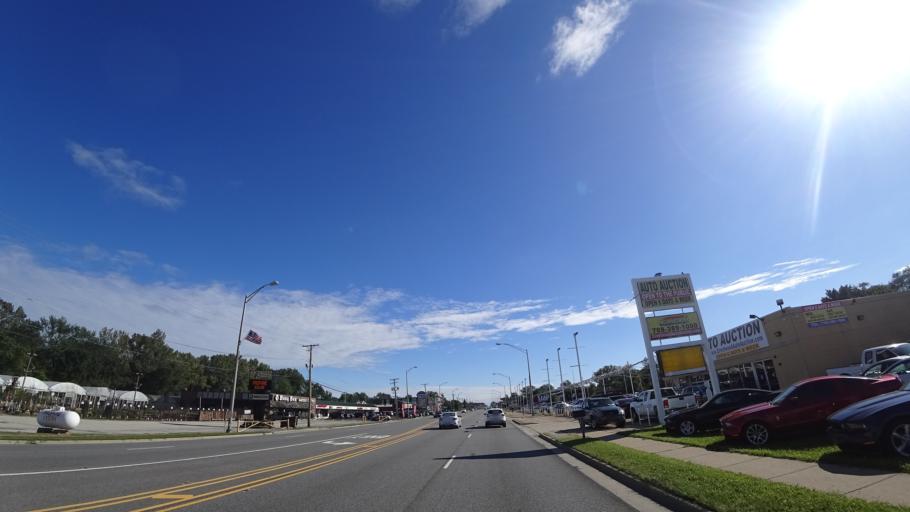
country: US
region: Illinois
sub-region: Cook County
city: Midlothian
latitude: 41.6363
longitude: -87.7378
